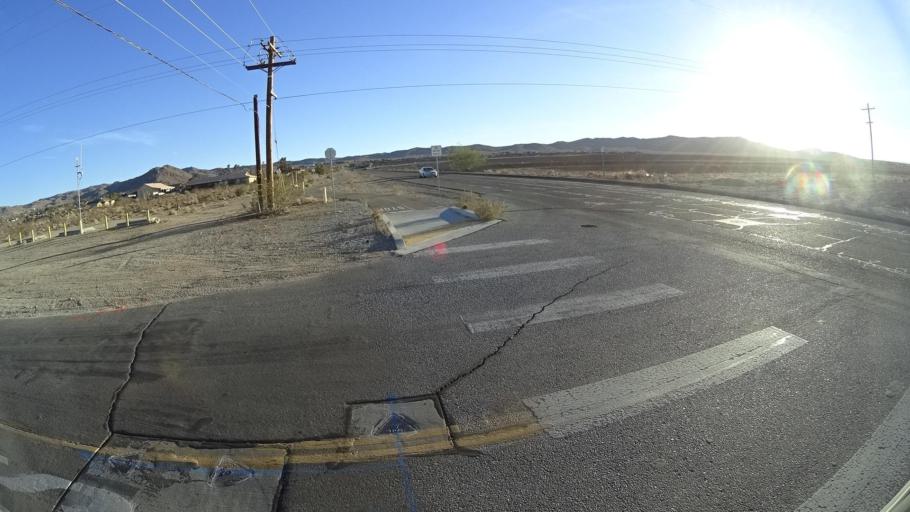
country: US
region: California
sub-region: Kern County
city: Ridgecrest
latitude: 35.5937
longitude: -117.6702
